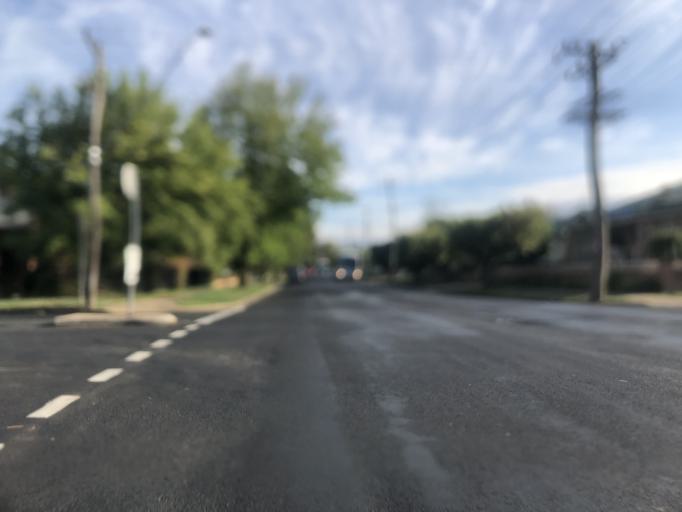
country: AU
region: New South Wales
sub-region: Orange Municipality
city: Orange
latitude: -33.2923
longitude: 149.0970
